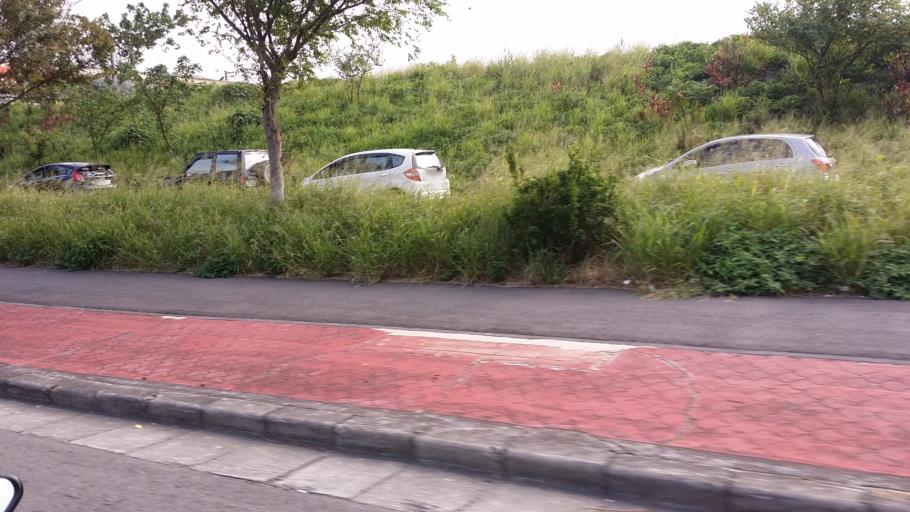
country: TW
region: Taiwan
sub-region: Hsinchu
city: Zhubei
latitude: 24.8248
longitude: 120.9992
